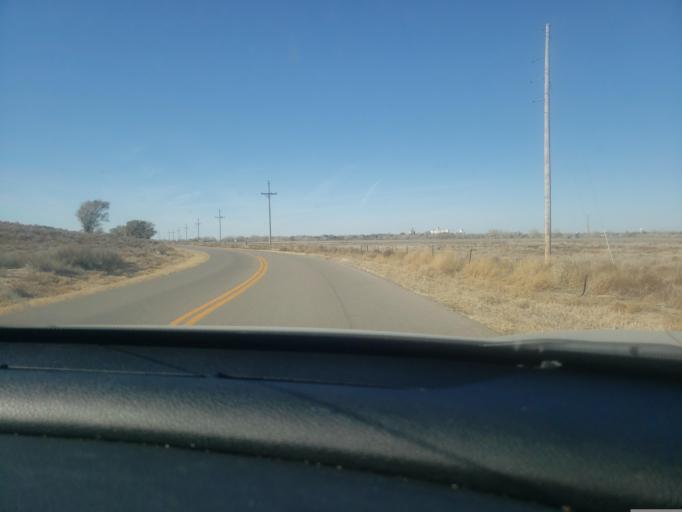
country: US
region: Kansas
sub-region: Finney County
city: Garden City
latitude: 37.9506
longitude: -100.8543
